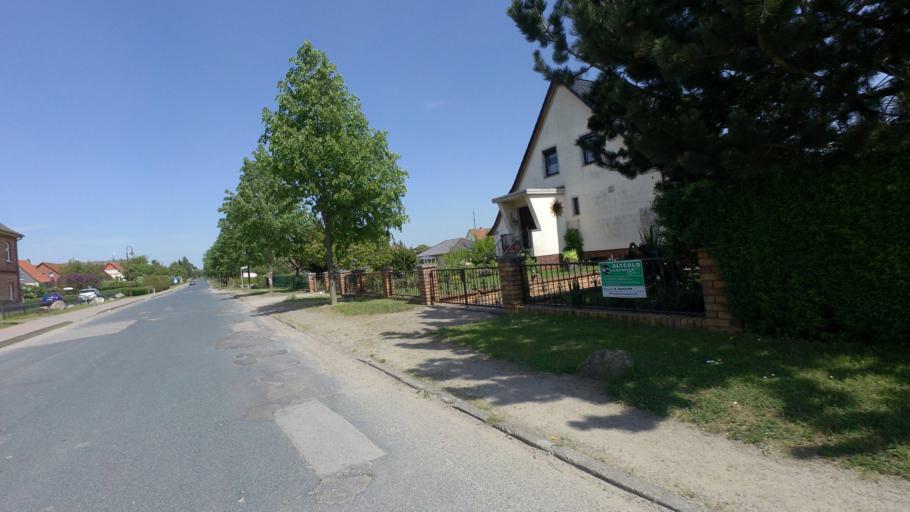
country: DE
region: Mecklenburg-Vorpommern
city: Mollenhagen
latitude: 53.5234
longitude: 12.9287
